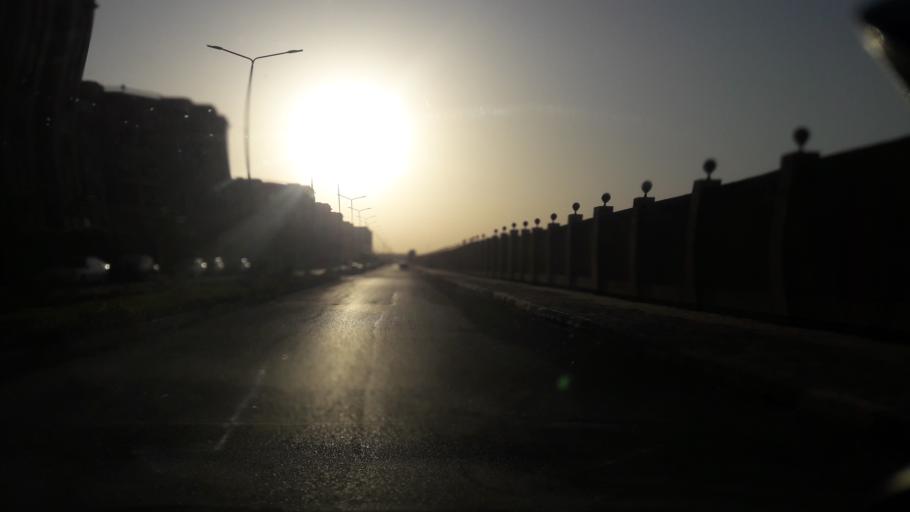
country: EG
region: Al Jizah
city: Madinat Sittah Uktubar
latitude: 29.9578
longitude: 31.0451
